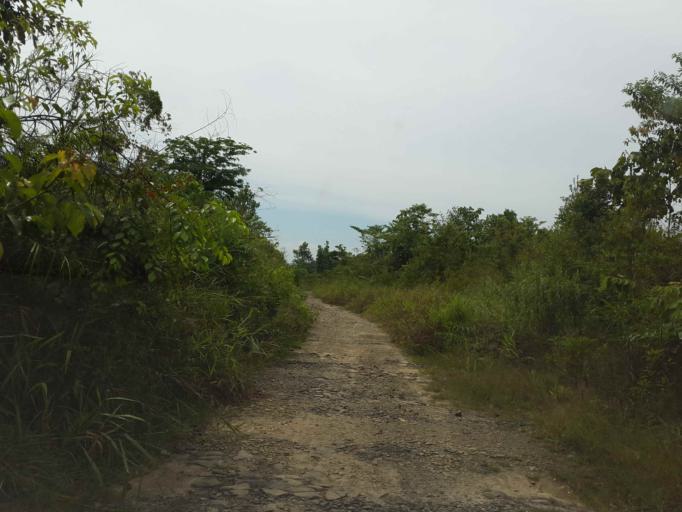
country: MY
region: Sarawak
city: Kuching
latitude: 1.2722
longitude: 109.8232
